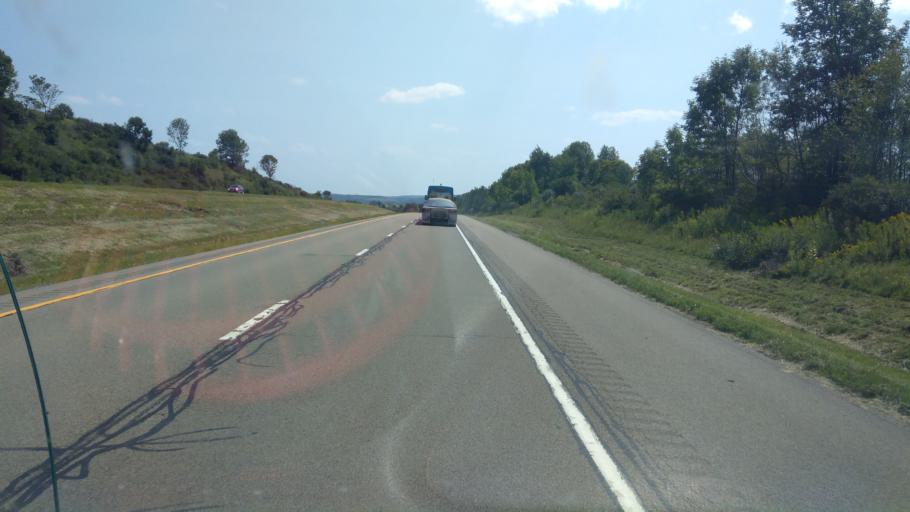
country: US
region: New York
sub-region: Steuben County
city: Canisteo
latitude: 42.3734
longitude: -77.5245
